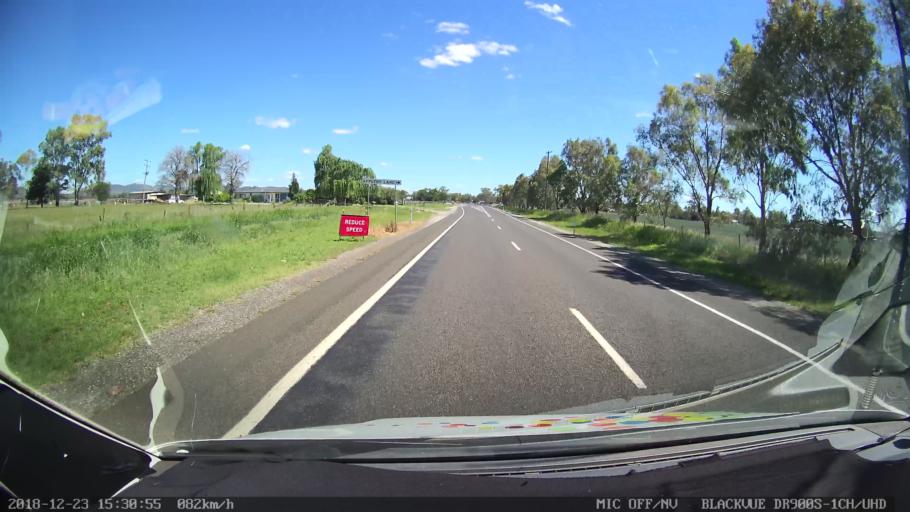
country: AU
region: New South Wales
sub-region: Tamworth Municipality
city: East Tamworth
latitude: -30.9652
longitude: 150.8663
